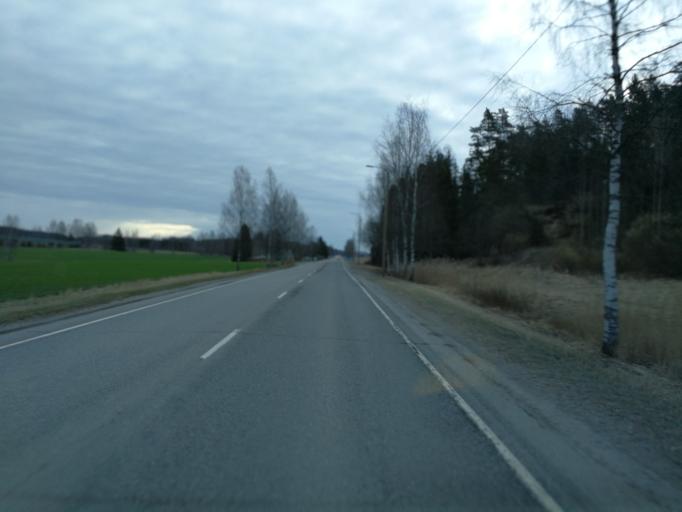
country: FI
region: Varsinais-Suomi
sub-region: Turku
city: Piikkioe
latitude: 60.4260
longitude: 22.5364
